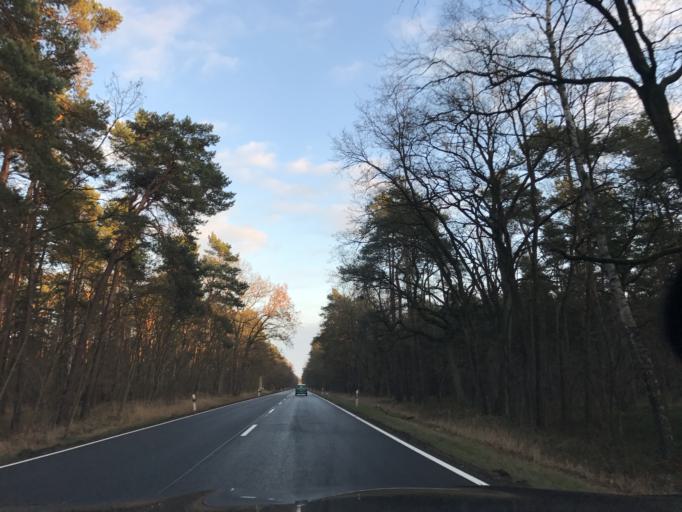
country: DE
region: Brandenburg
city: Bensdorf
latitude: 52.4112
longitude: 12.2821
